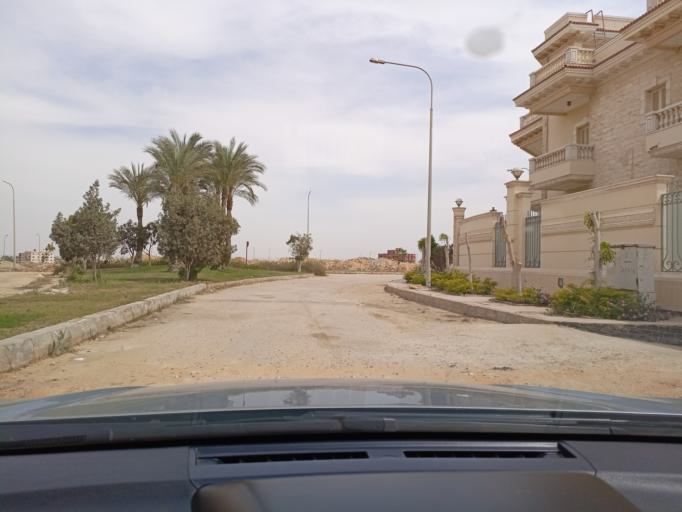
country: EG
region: Muhafazat al Qalyubiyah
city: Al Khankah
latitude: 30.2491
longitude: 31.5051
